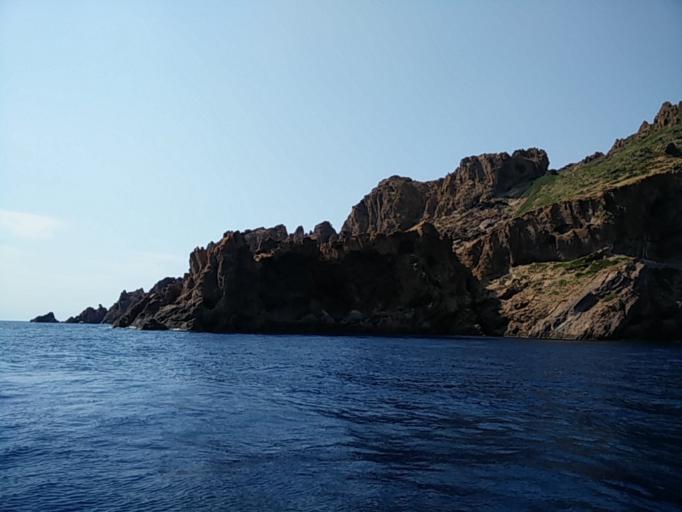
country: FR
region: Corsica
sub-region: Departement de la Corse-du-Sud
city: Cargese
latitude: 42.3318
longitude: 8.5600
